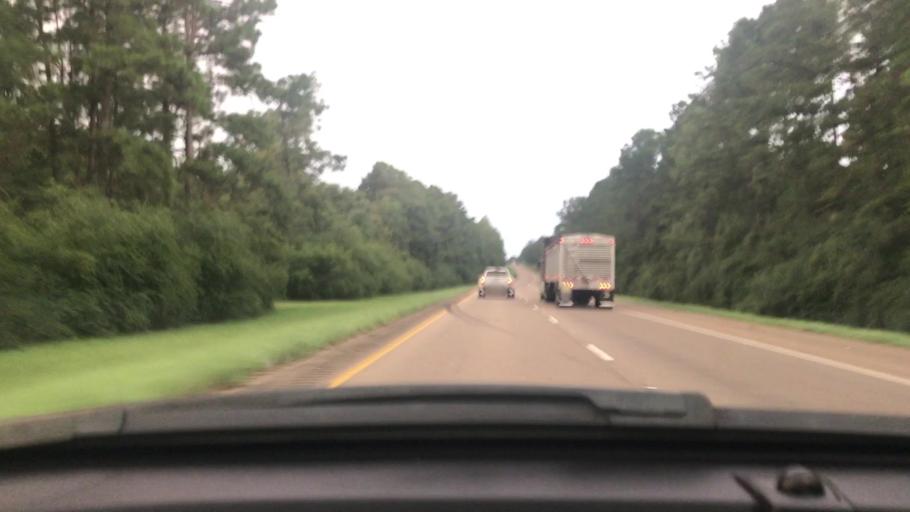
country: US
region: Louisiana
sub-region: Tangipahoa Parish
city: Roseland
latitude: 30.8519
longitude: -90.5333
